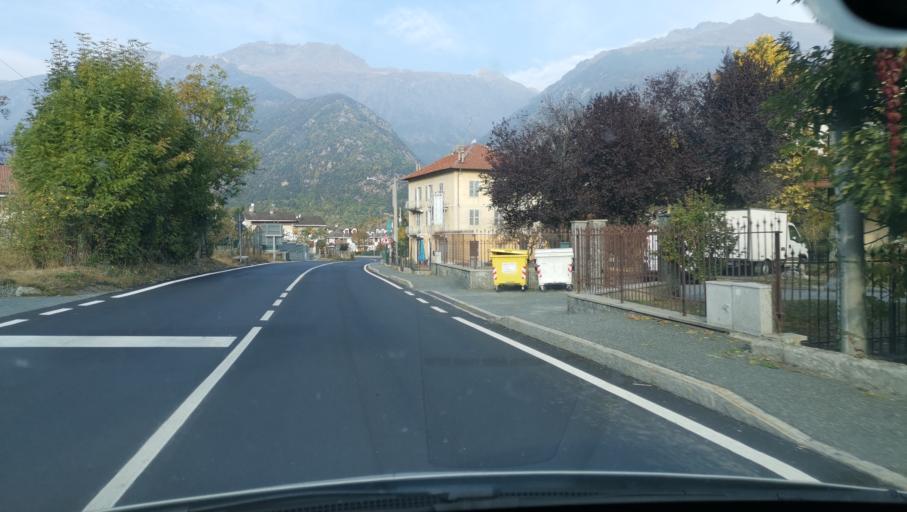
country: IT
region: Piedmont
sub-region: Provincia di Torino
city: Gravere
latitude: 45.1269
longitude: 7.0163
